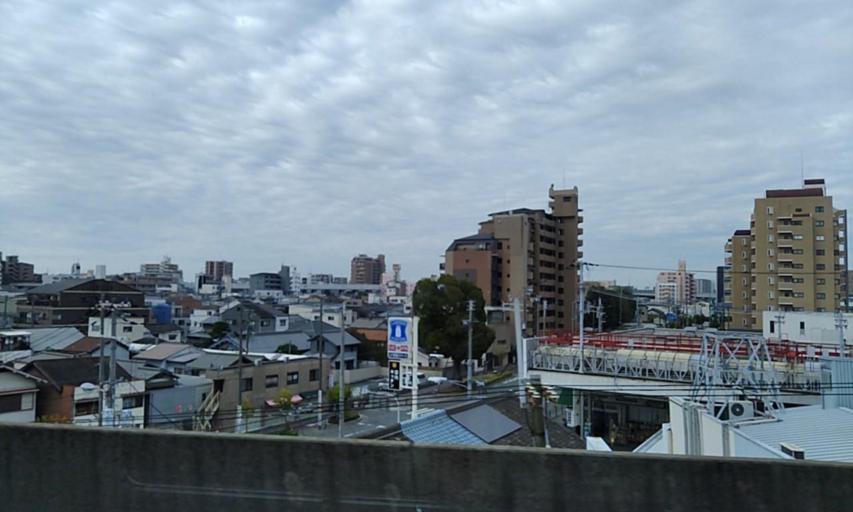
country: JP
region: Osaka
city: Matsubara
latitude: 34.6313
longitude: 135.5292
